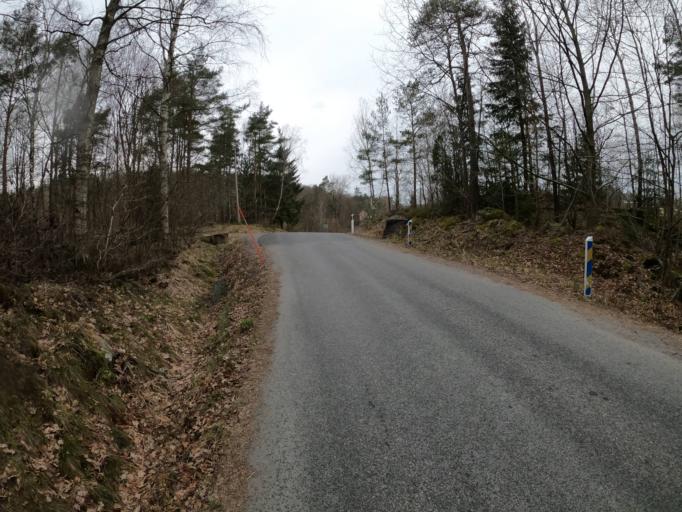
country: SE
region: Vaestra Goetaland
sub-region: Harryda Kommun
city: Molnlycke
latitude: 57.6412
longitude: 12.1065
